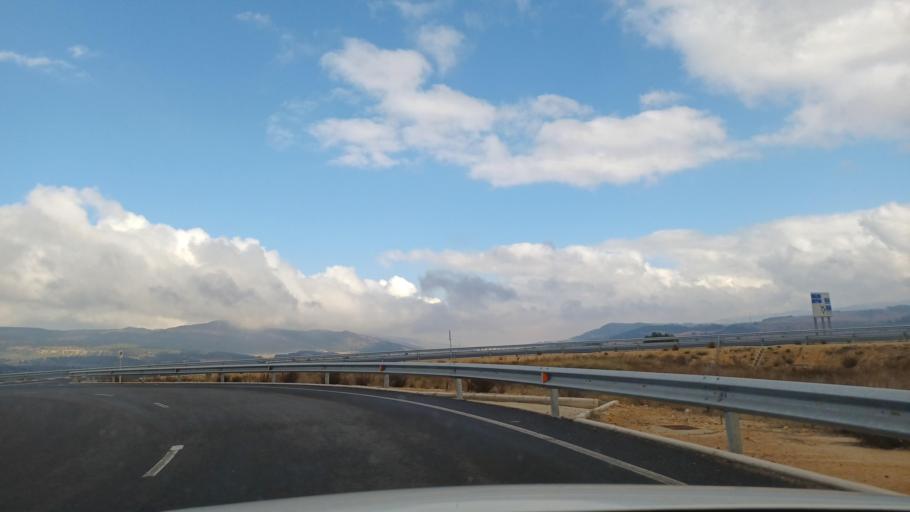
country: ES
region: Valencia
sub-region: Provincia de Valencia
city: La Font de la Figuera
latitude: 38.8165
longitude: -0.8870
